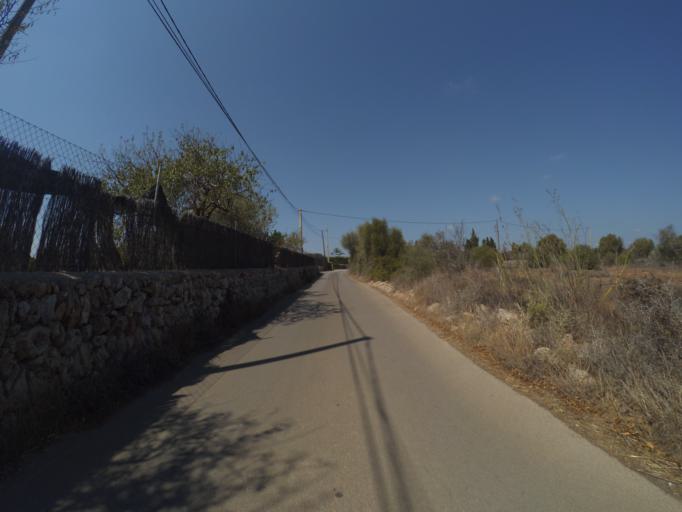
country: ES
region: Balearic Islands
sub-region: Illes Balears
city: Santanyi
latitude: 39.3907
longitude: 3.2378
